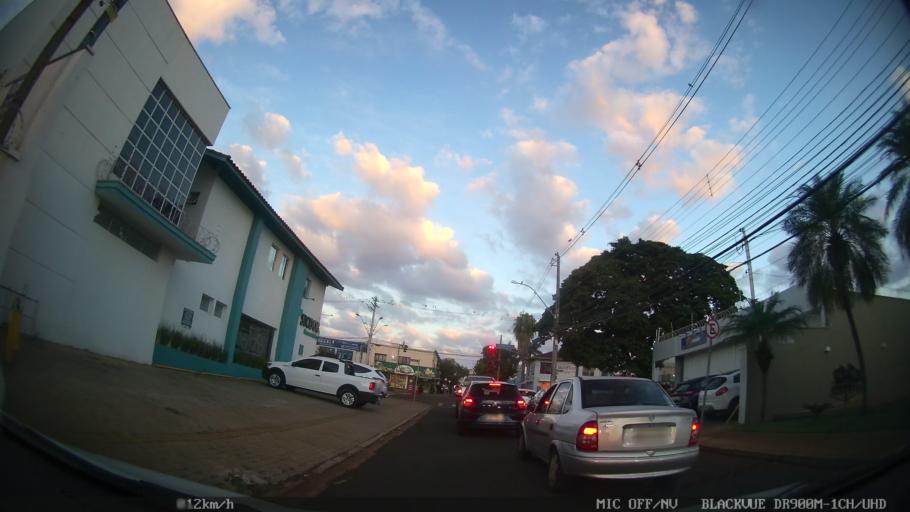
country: BR
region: Sao Paulo
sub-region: Ribeirao Preto
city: Ribeirao Preto
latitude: -21.1886
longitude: -47.8082
